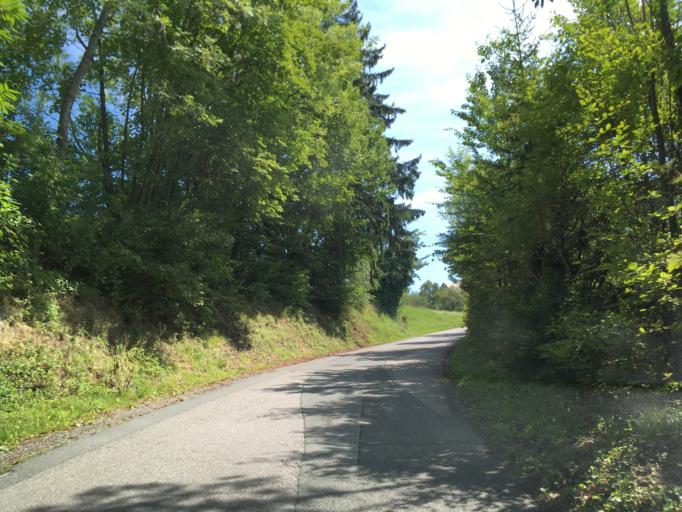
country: AT
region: Styria
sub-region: Politischer Bezirk Leibnitz
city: Kitzeck im Sausal
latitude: 46.7884
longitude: 15.4212
